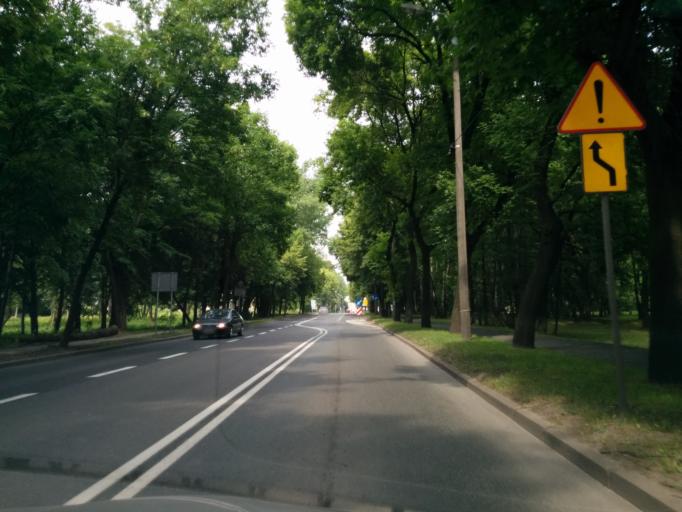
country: PL
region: Silesian Voivodeship
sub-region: Ruda Slaska
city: Ruda Slaska
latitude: 50.2747
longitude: 18.8505
